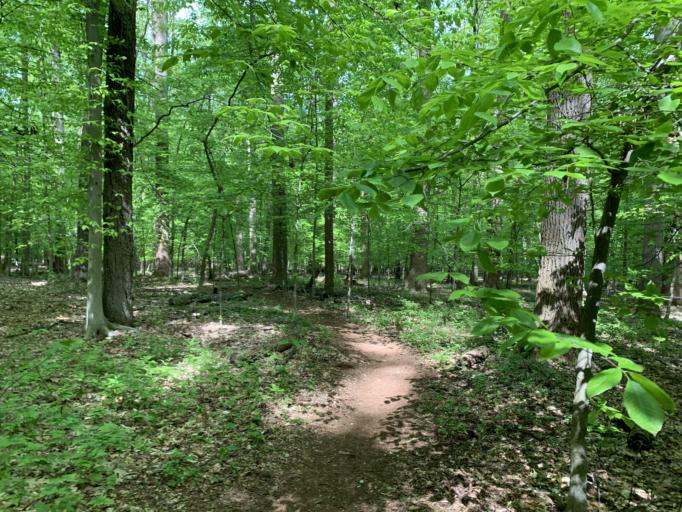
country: US
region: Maryland
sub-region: Harford County
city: South Bel Air
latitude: 39.6197
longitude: -76.2739
